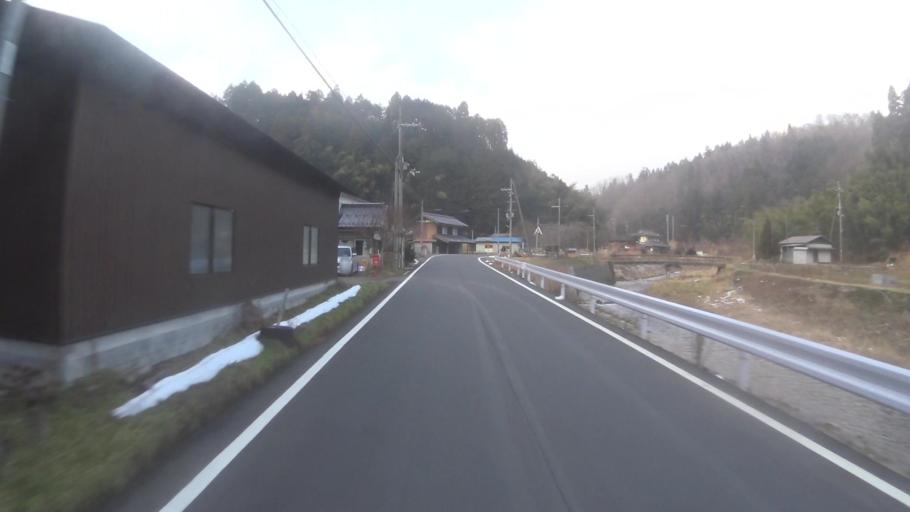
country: JP
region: Kyoto
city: Maizuru
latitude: 35.4294
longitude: 135.4781
